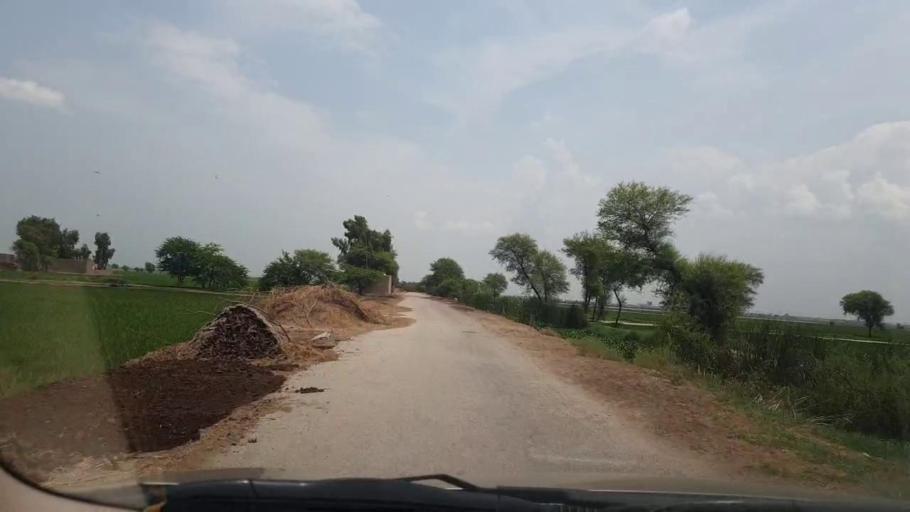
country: PK
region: Sindh
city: Larkana
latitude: 27.6077
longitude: 68.1579
